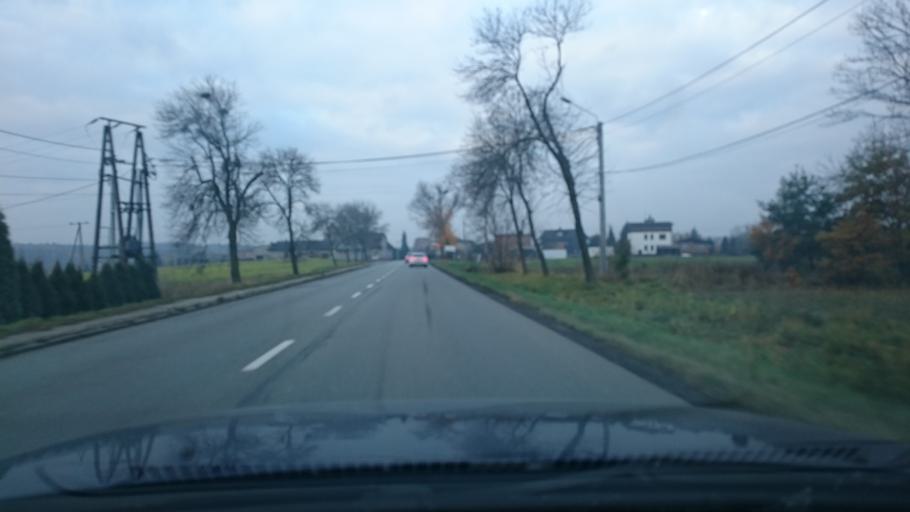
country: PL
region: Silesian Voivodeship
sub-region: Powiat rybnicki
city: Stanowice
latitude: 50.1222
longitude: 18.6411
